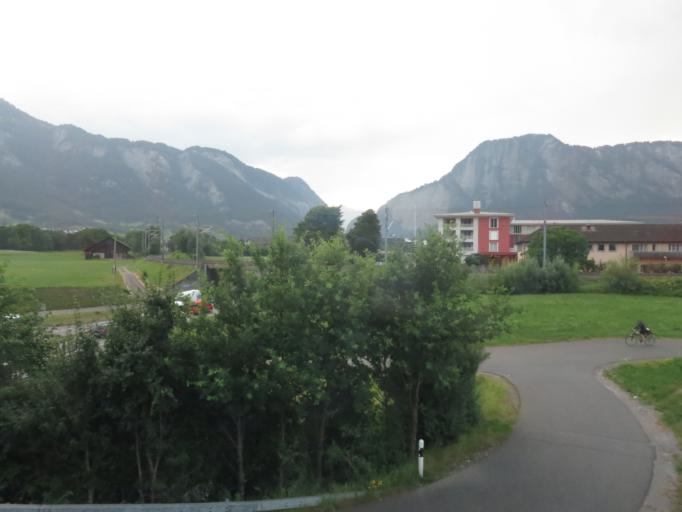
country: CH
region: Grisons
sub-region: Landquart District
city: Malans
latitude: 46.9709
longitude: 9.5530
